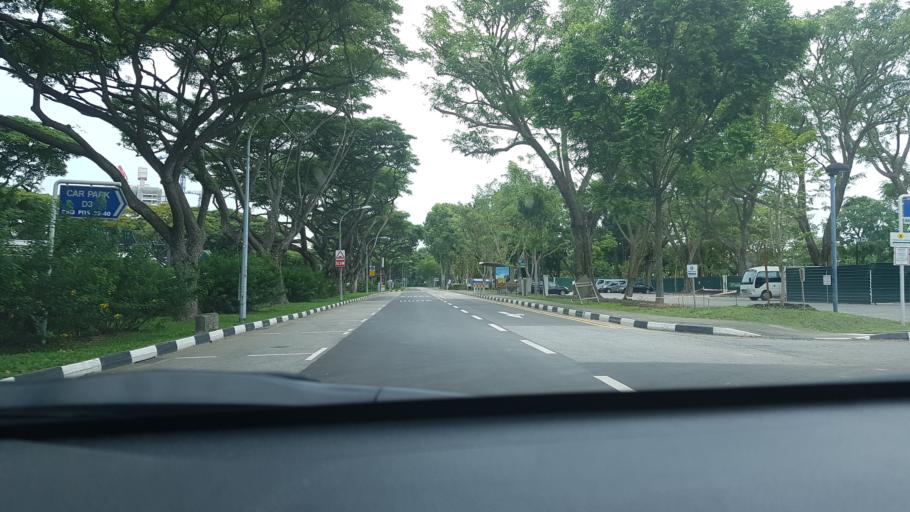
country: SG
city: Singapore
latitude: 1.3047
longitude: 103.9230
